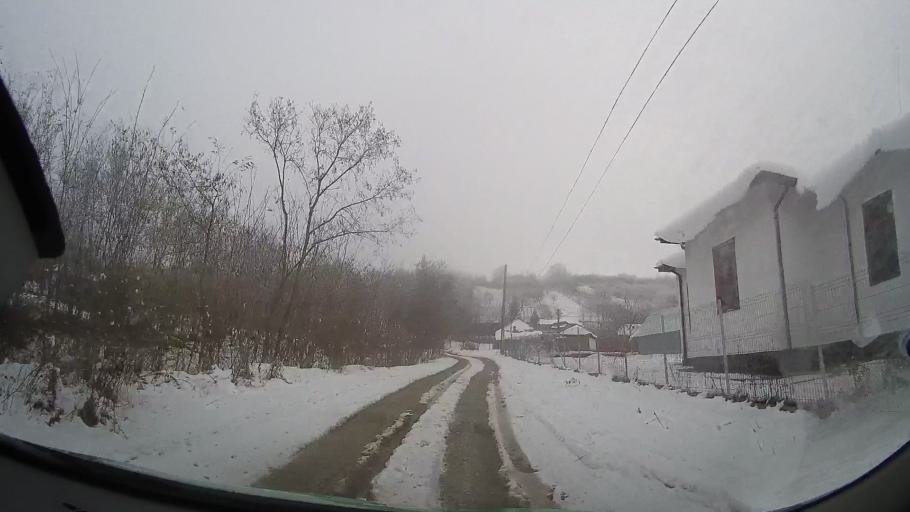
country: RO
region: Bacau
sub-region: Comuna Vultureni
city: Vultureni
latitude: 46.3792
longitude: 27.2862
